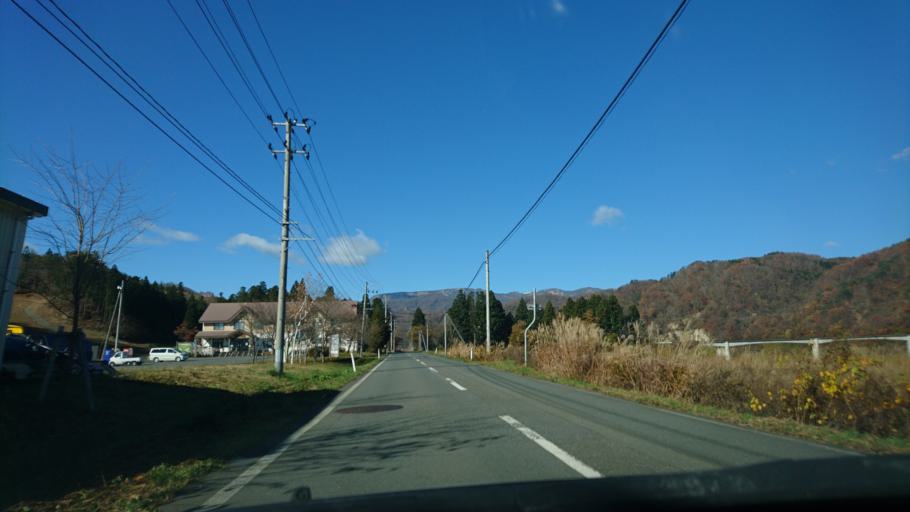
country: JP
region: Iwate
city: Mizusawa
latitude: 39.1179
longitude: 140.9392
